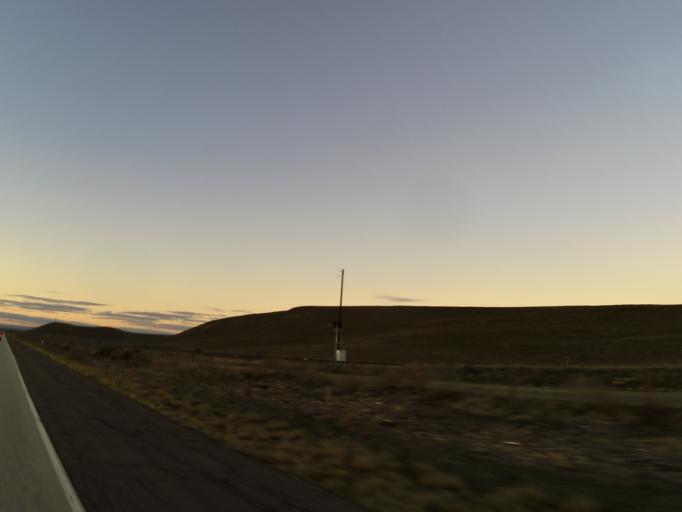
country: US
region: California
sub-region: Monterey County
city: King City
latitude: 36.1460
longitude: -121.0396
